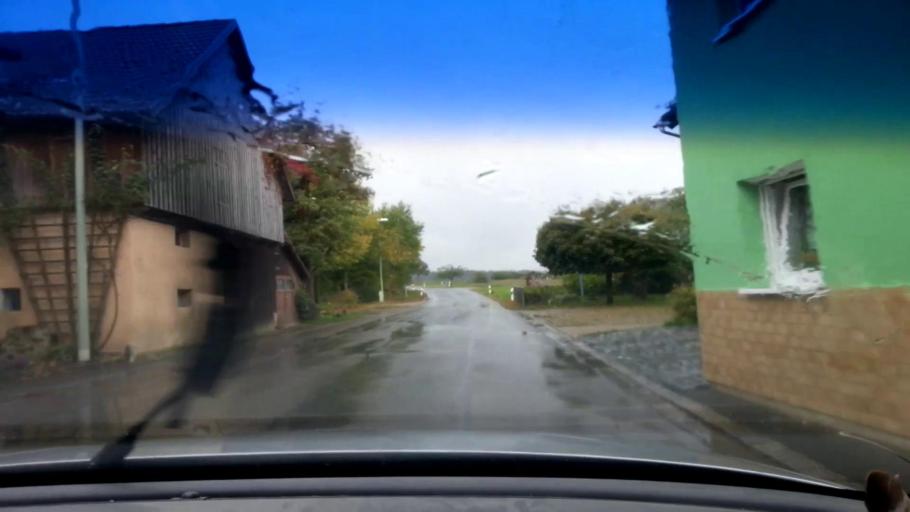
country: DE
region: Bavaria
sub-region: Upper Franconia
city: Altendorf
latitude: 50.0428
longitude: 11.1747
